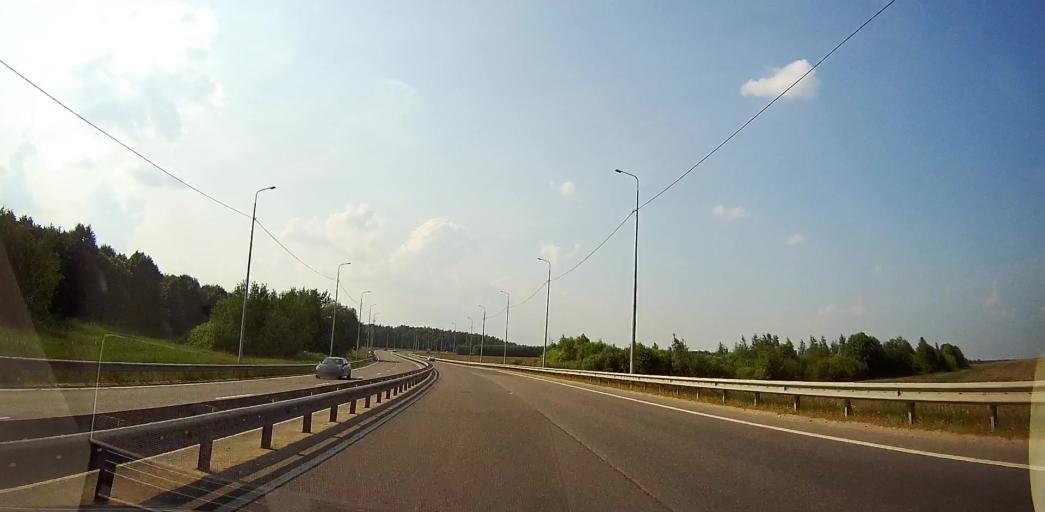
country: RU
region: Moskovskaya
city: Vostryakovo
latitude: 55.4161
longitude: 37.8559
